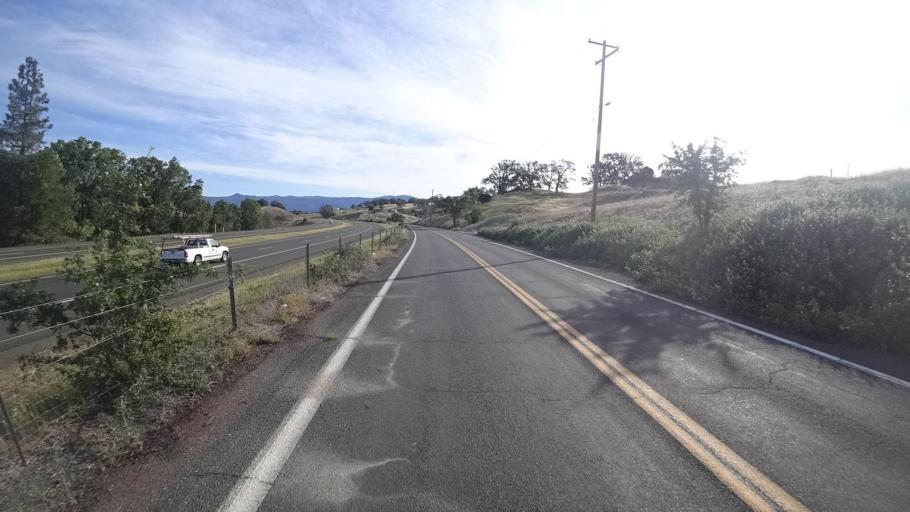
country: US
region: California
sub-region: Lake County
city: North Lakeport
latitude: 39.0904
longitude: -122.9168
